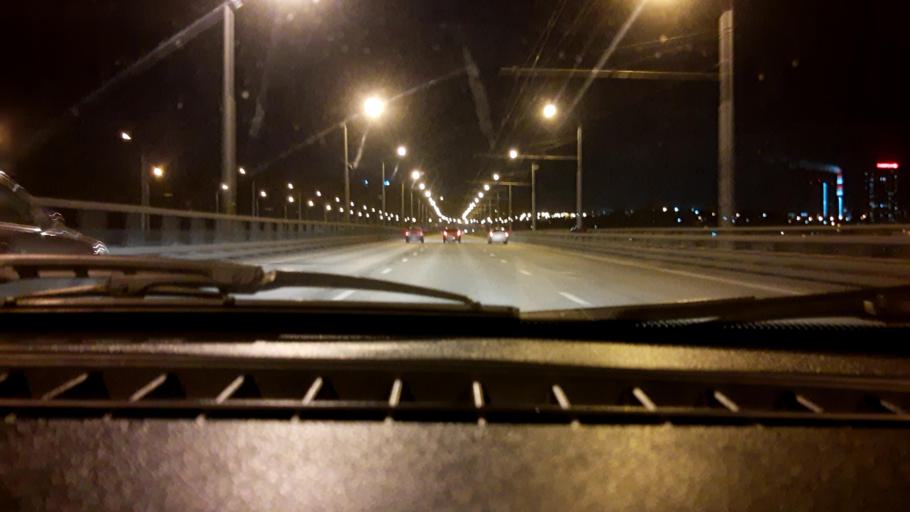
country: RU
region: Bashkortostan
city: Ufa
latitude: 54.7587
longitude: 55.9624
